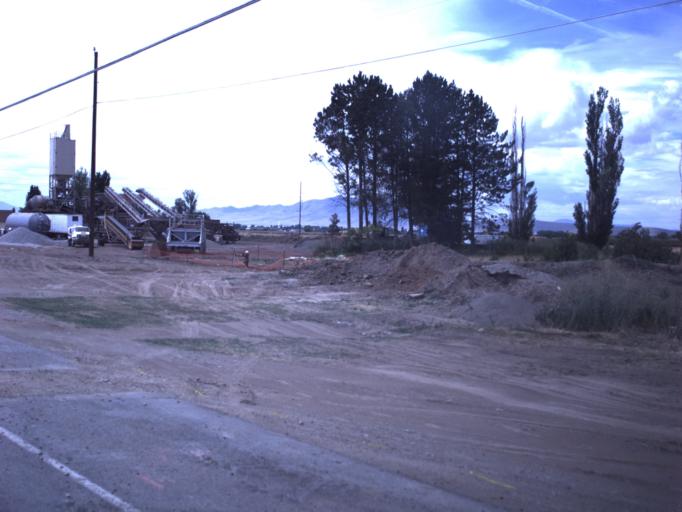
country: US
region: Utah
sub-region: Davis County
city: West Point
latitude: 41.1138
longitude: -112.0646
